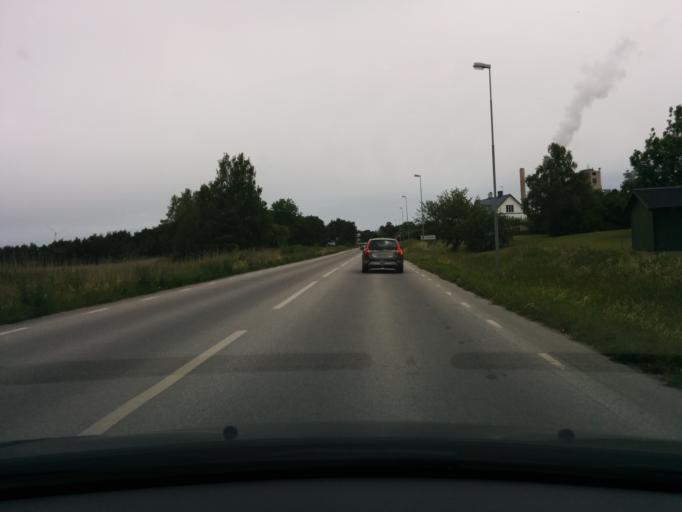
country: SE
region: Gotland
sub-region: Gotland
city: Slite
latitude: 57.7010
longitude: 18.7952
